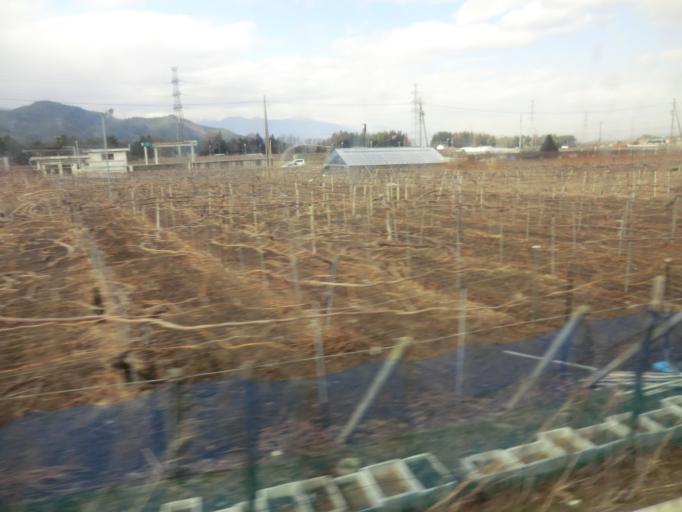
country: JP
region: Nagano
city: Shiojiri
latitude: 36.0945
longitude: 137.9248
